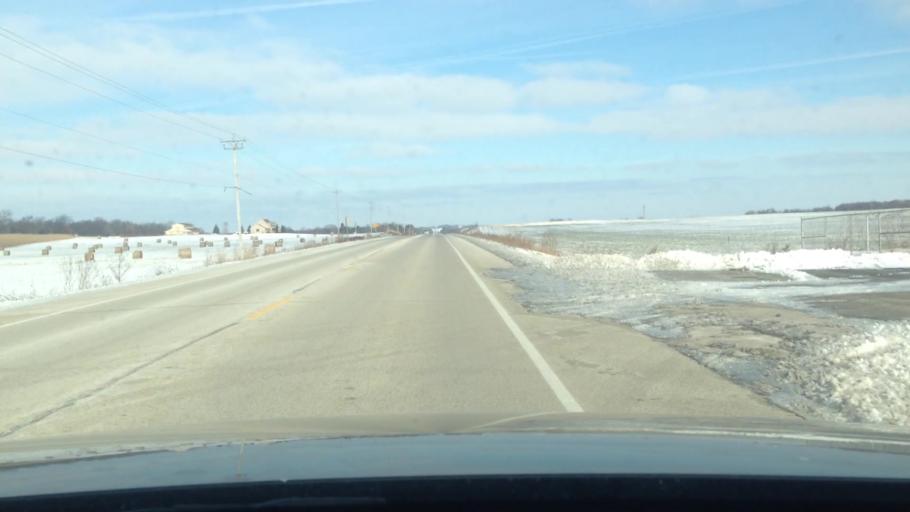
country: US
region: Wisconsin
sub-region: Walworth County
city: East Troy
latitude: 42.6942
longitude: -88.4048
